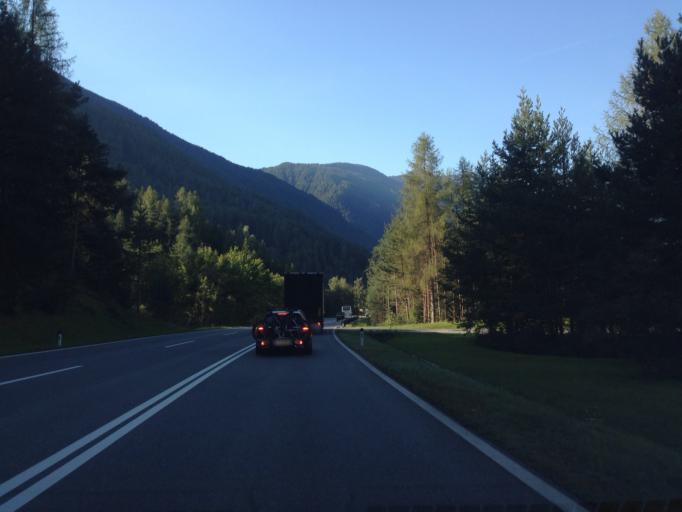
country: AT
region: Tyrol
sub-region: Politischer Bezirk Imst
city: Nassereith
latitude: 47.3048
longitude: 10.8591
